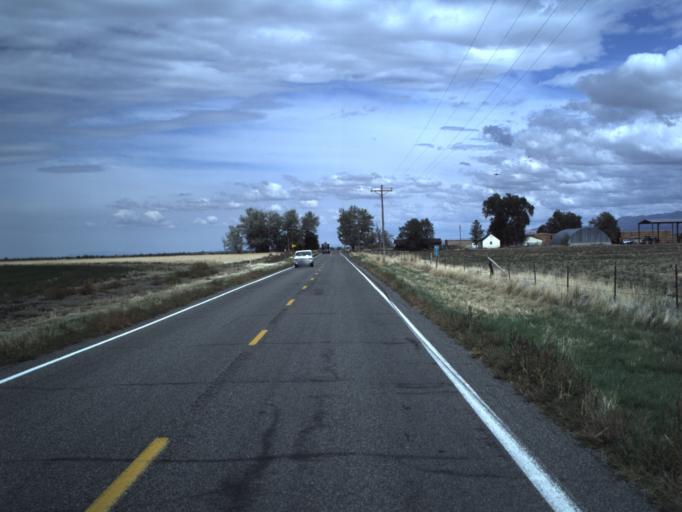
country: US
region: Utah
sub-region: Millard County
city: Fillmore
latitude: 39.0556
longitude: -112.4098
